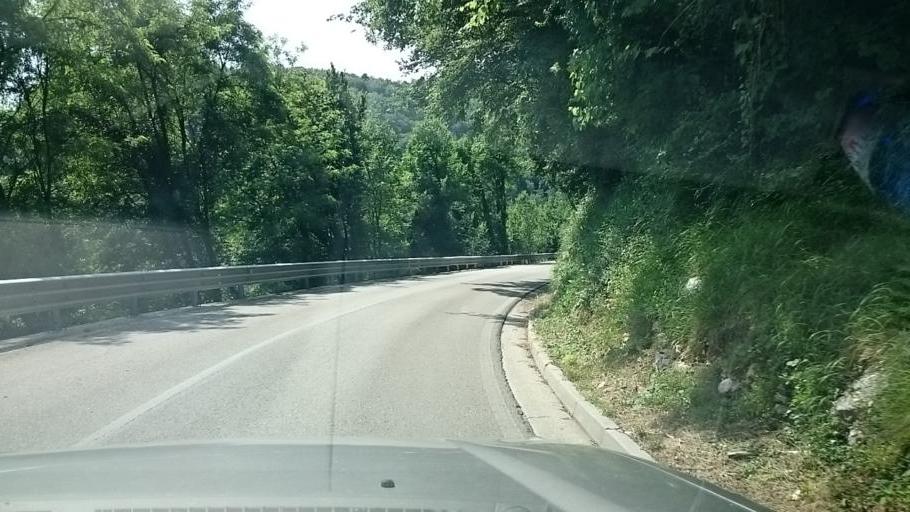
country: IT
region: Veneto
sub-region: Provincia di Vicenza
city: Conco
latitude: 45.7826
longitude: 11.6026
